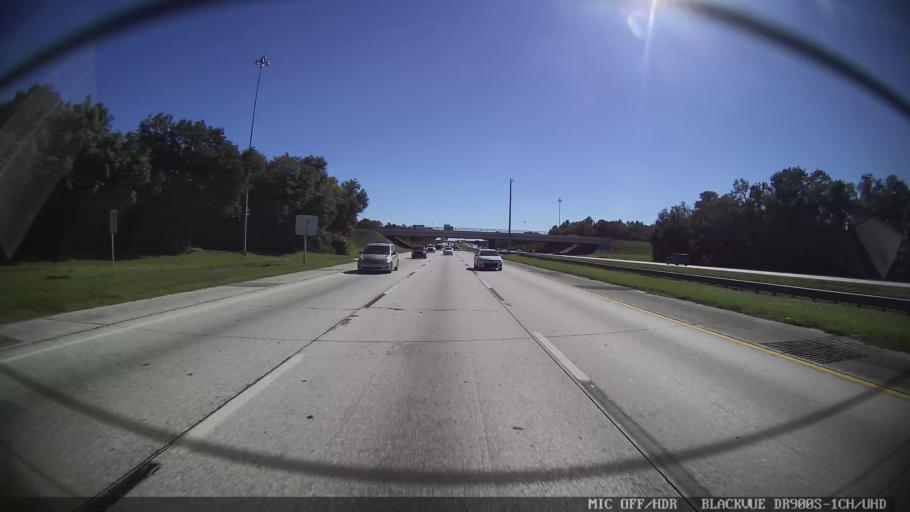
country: US
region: Florida
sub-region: Hillsborough County
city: Mango
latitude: 27.9885
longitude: -82.3256
